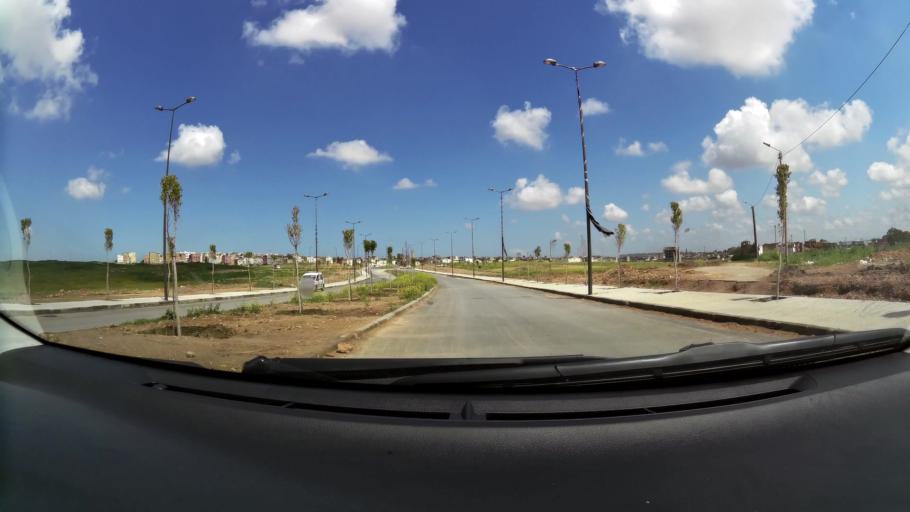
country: MA
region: Grand Casablanca
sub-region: Mediouna
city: Tit Mellil
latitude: 33.5387
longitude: -7.5457
